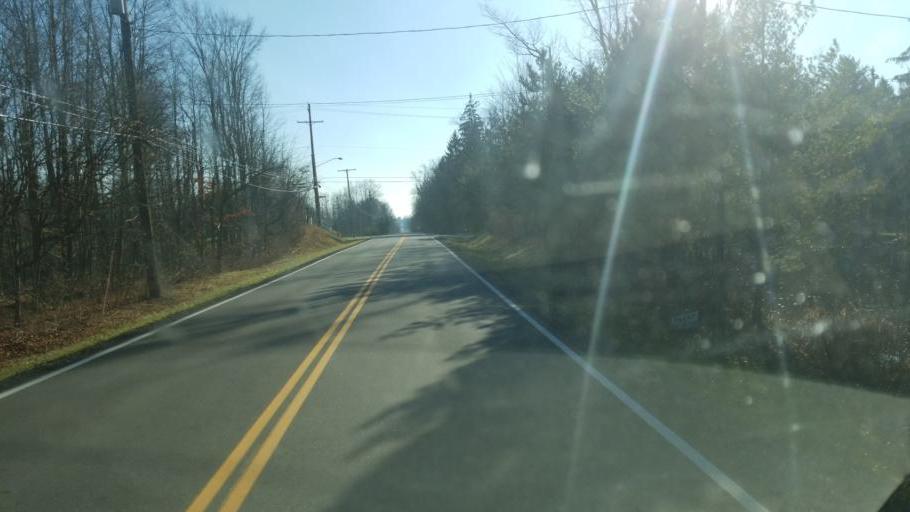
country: US
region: Ohio
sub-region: Geauga County
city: Bainbridge
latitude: 41.3783
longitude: -81.2463
